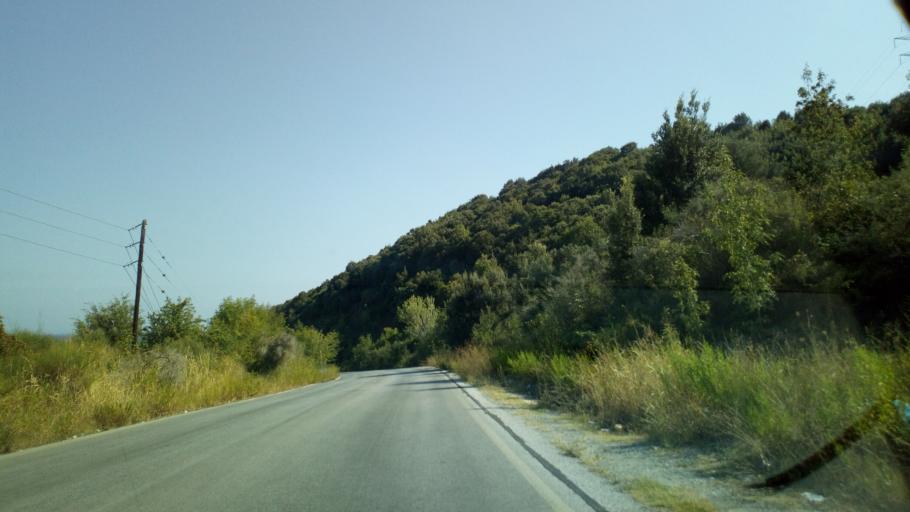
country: GR
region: Central Macedonia
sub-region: Nomos Thessalonikis
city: Stavros
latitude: 40.6527
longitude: 23.7405
